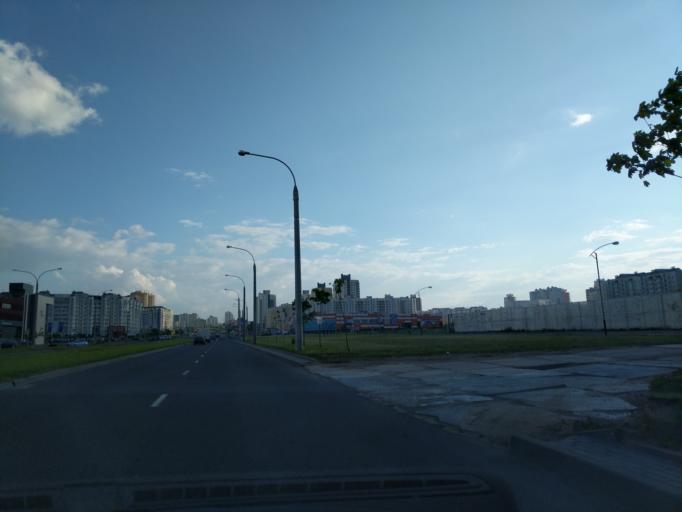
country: BY
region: Minsk
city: Zhdanovichy
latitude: 53.9291
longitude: 27.4440
